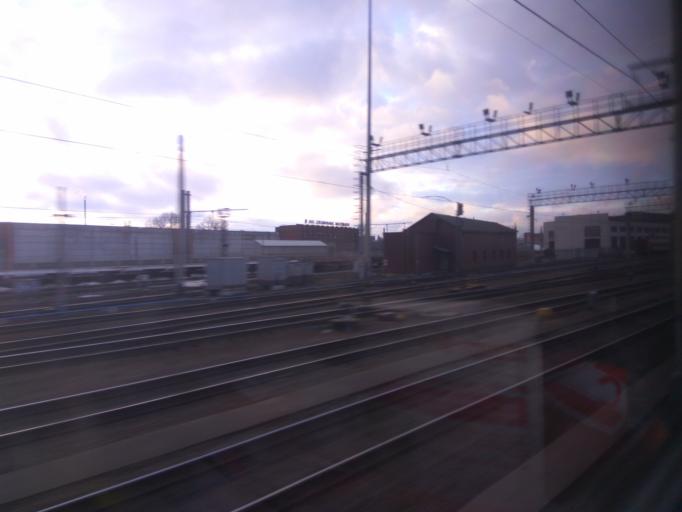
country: RU
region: St.-Petersburg
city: Centralniy
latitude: 59.9082
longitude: 30.3713
